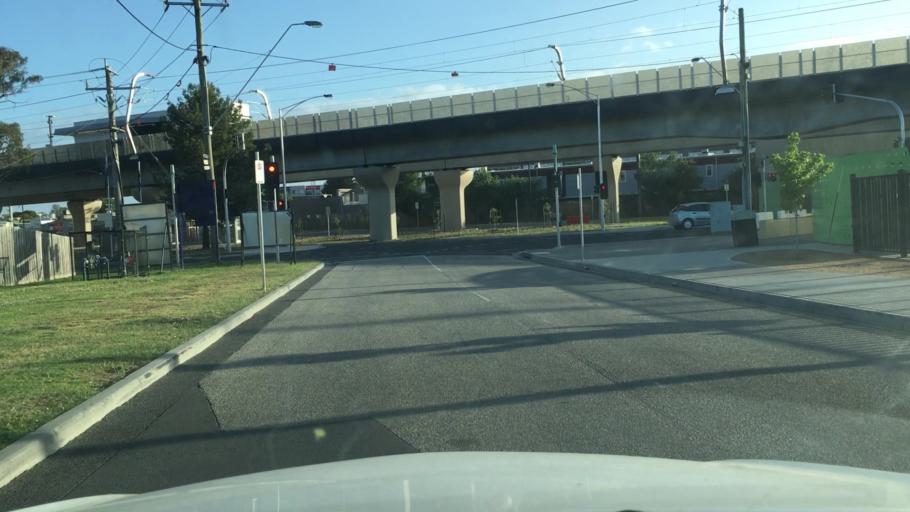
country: AU
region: Victoria
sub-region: Greater Dandenong
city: Noble Park
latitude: -37.9648
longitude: 145.1751
